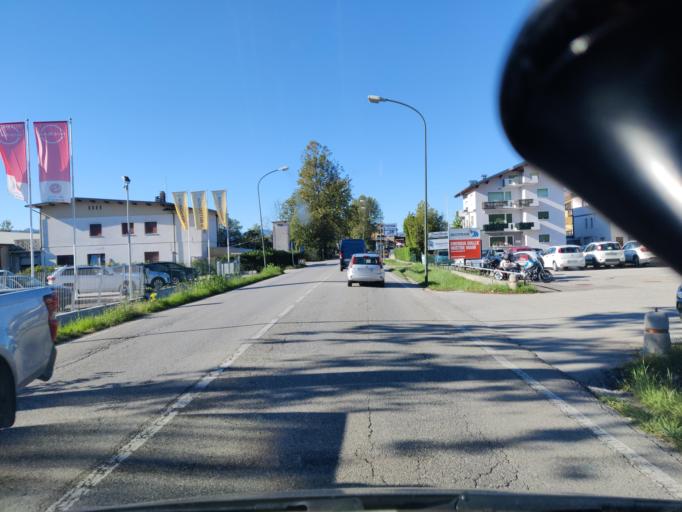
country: IT
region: Veneto
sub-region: Provincia di Belluno
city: Belluno
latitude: 46.1568
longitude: 12.2349
